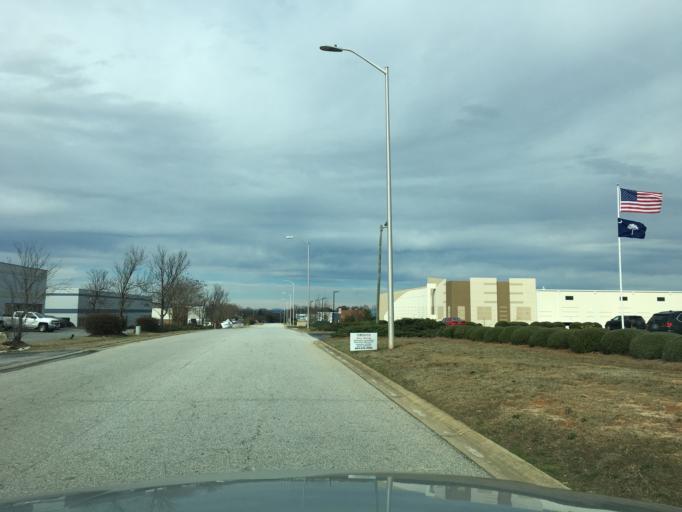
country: US
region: South Carolina
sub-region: Spartanburg County
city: Duncan
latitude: 34.9064
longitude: -82.1857
